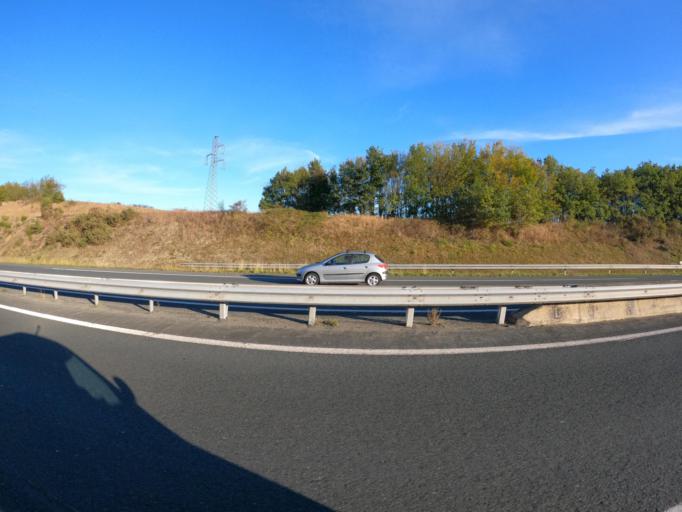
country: FR
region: Pays de la Loire
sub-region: Departement de Maine-et-Loire
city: La Tessoualle
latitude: 47.0243
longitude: -0.8666
